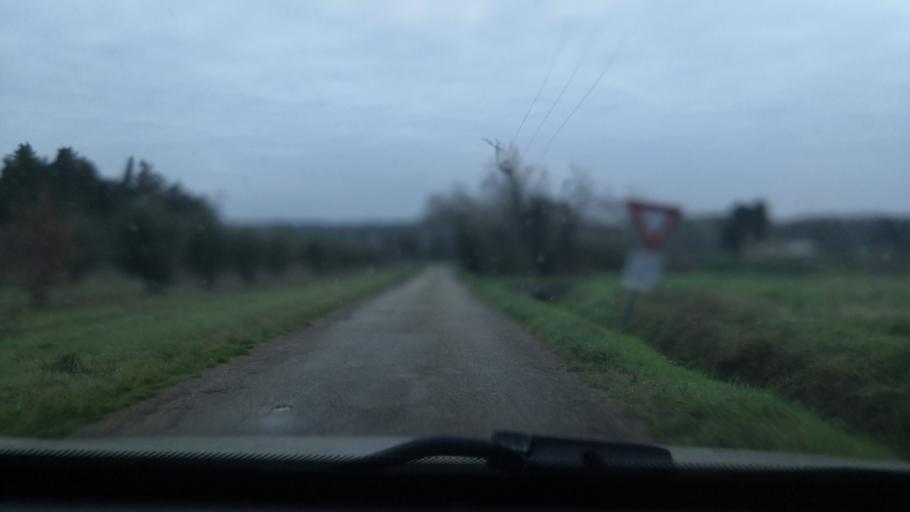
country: FR
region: Rhone-Alpes
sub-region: Departement de la Drome
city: Montelimar
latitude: 44.5273
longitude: 4.7510
